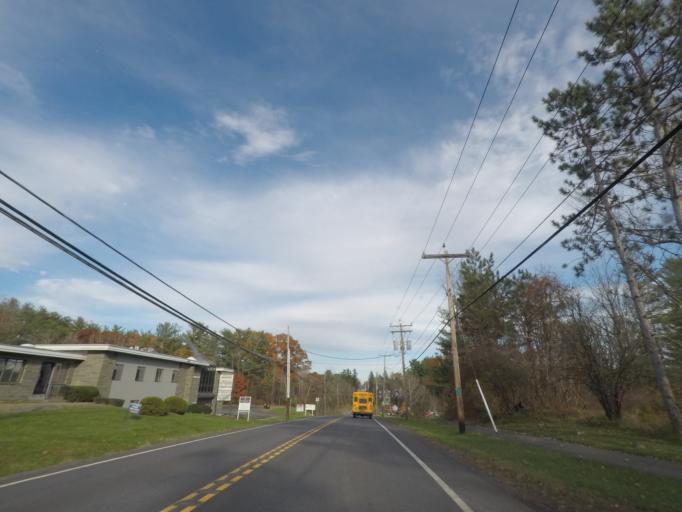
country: US
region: New York
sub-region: Albany County
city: Delmar
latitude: 42.6110
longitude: -73.8638
